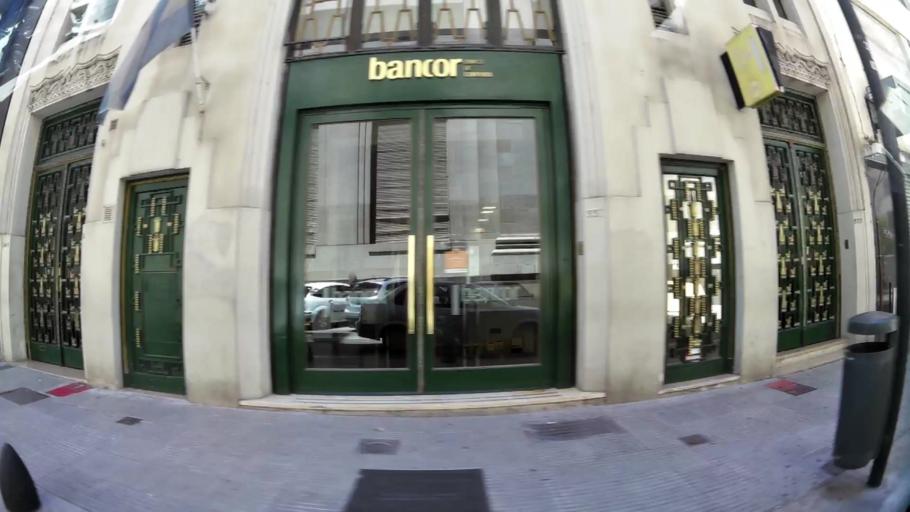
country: AR
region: Buenos Aires F.D.
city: Buenos Aires
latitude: -34.6066
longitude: -58.3717
